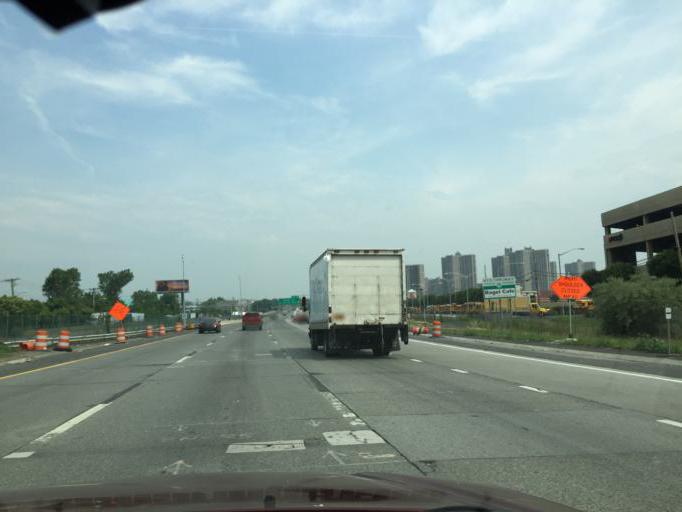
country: US
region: New York
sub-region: Bronx
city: Eastchester
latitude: 40.8628
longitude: -73.8294
